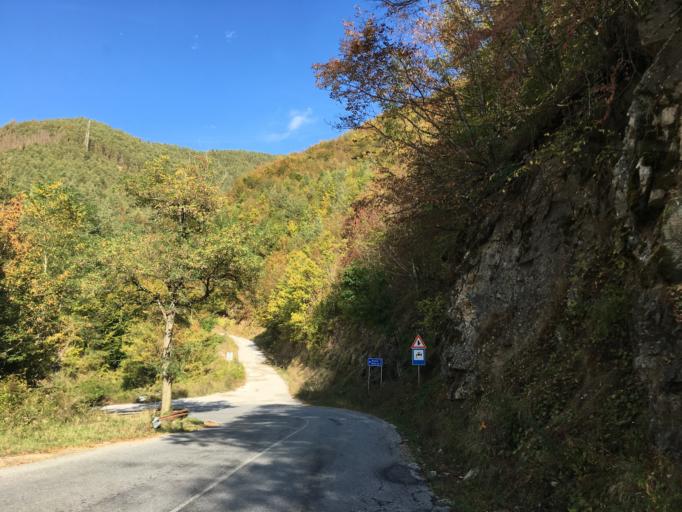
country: BG
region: Smolyan
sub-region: Obshtina Madan
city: Madan
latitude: 41.4588
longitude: 24.9752
